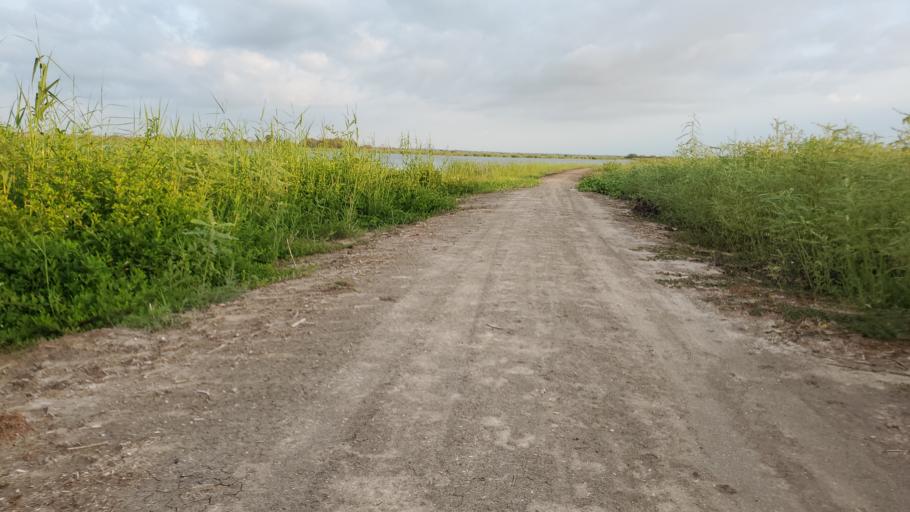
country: SN
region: Saint-Louis
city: Saint-Louis
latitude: 16.0163
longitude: -16.4009
